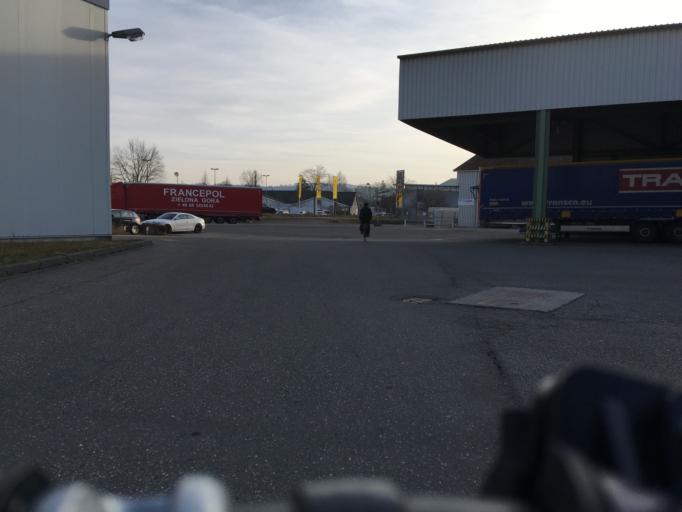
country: DE
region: Baden-Wuerttemberg
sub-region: Freiburg Region
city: Gottmadingen
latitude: 47.7376
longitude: 8.7874
